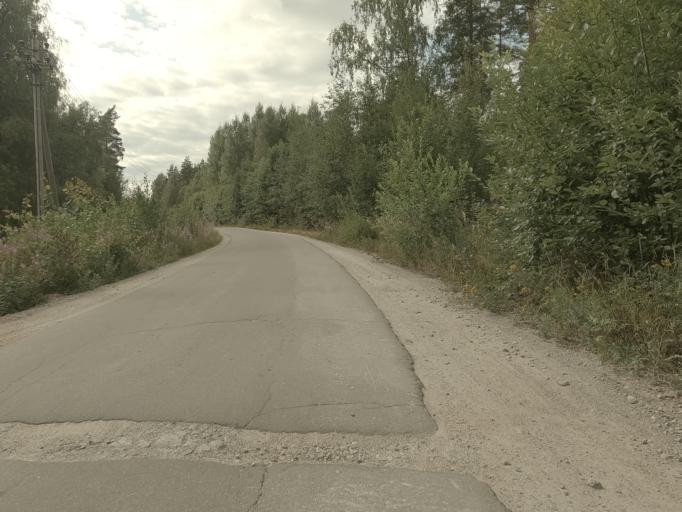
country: RU
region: Leningrad
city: Kamennogorsk
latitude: 60.9712
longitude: 29.1532
